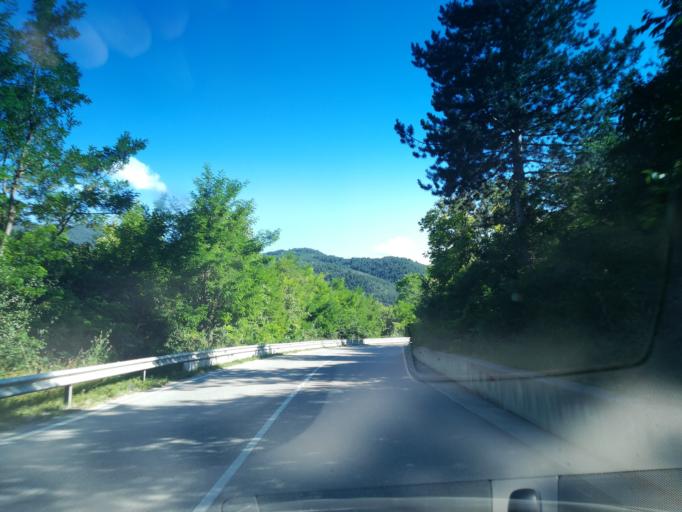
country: BG
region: Smolyan
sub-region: Obshtina Chepelare
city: Chepelare
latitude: 41.8603
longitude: 24.6875
